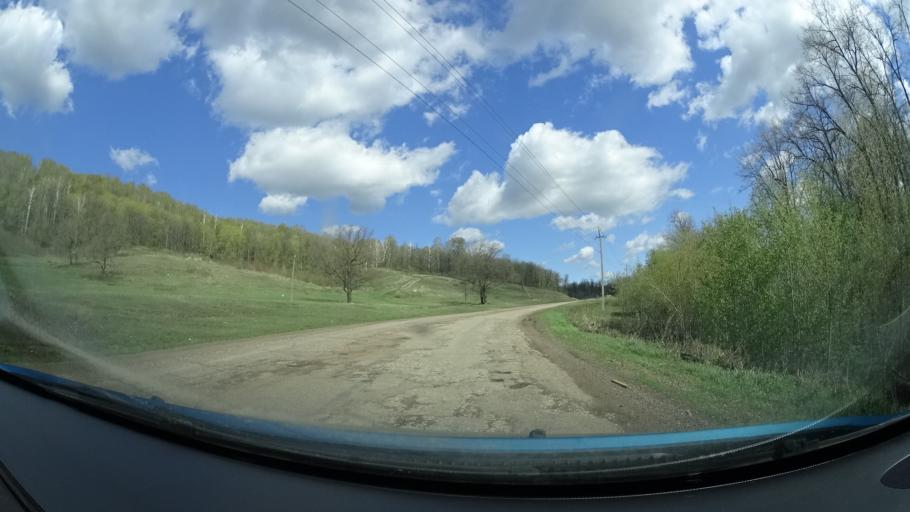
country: RU
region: Bashkortostan
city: Sterlitamak
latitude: 53.6897
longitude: 56.0968
